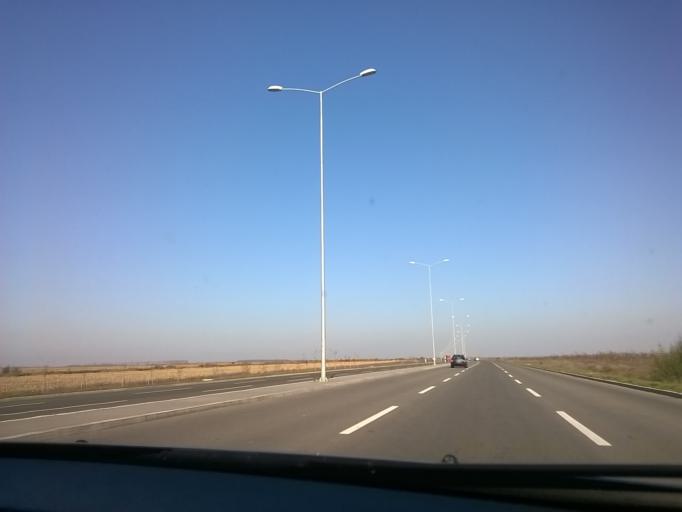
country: RS
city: Ovca
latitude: 44.8931
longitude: 20.5168
